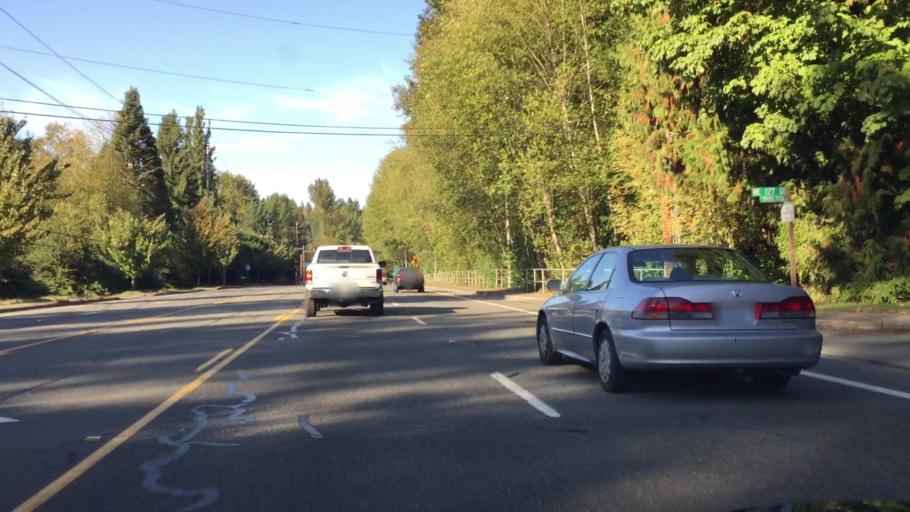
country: US
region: Washington
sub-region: King County
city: Cottage Lake
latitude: 47.7131
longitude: -122.0888
